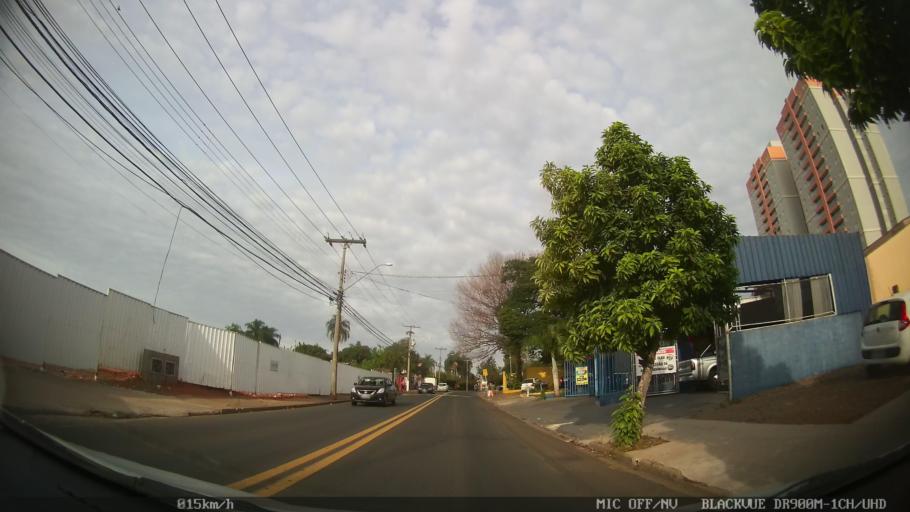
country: BR
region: Sao Paulo
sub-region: Piracicaba
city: Piracicaba
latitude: -22.7407
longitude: -47.6201
